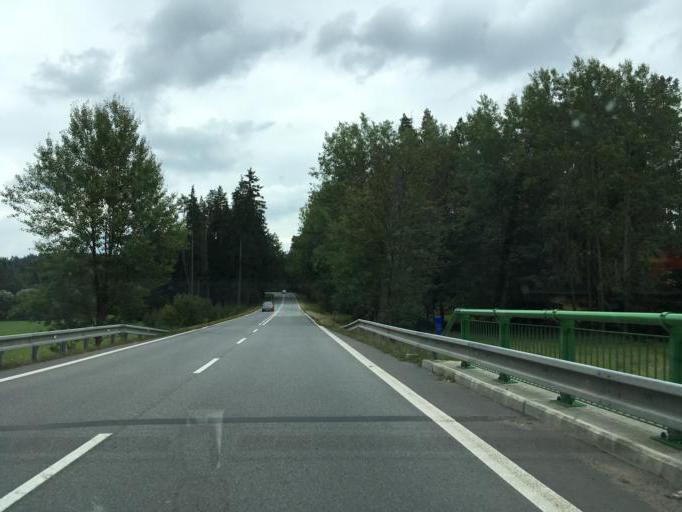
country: CZ
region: Vysocina
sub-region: Okres Pelhrimov
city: Pelhrimov
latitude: 49.4725
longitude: 15.1838
